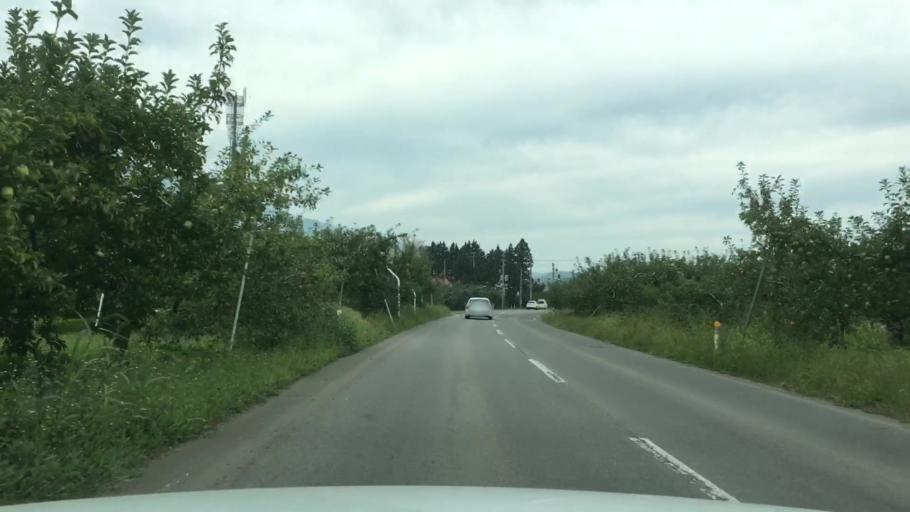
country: JP
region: Aomori
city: Hirosaki
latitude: 40.6441
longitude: 140.4271
